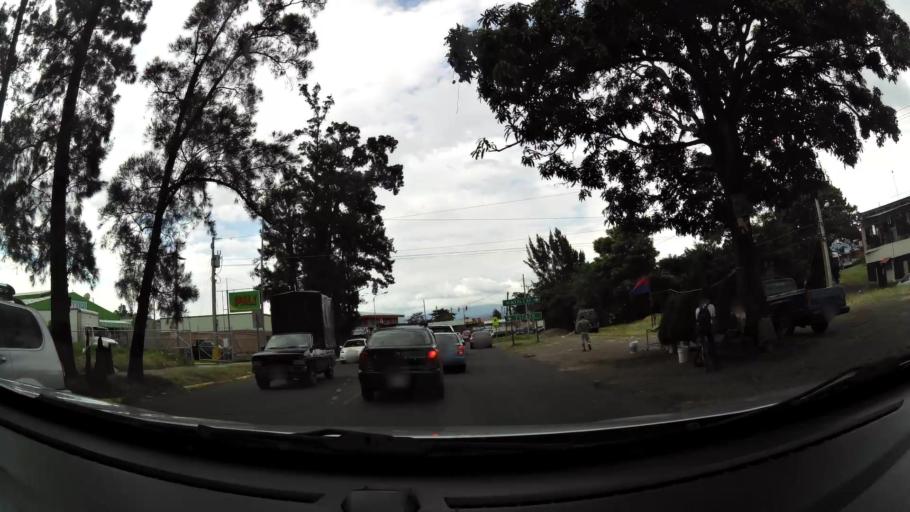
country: CR
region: San Jose
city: San Felipe
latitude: 9.9169
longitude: -84.1170
